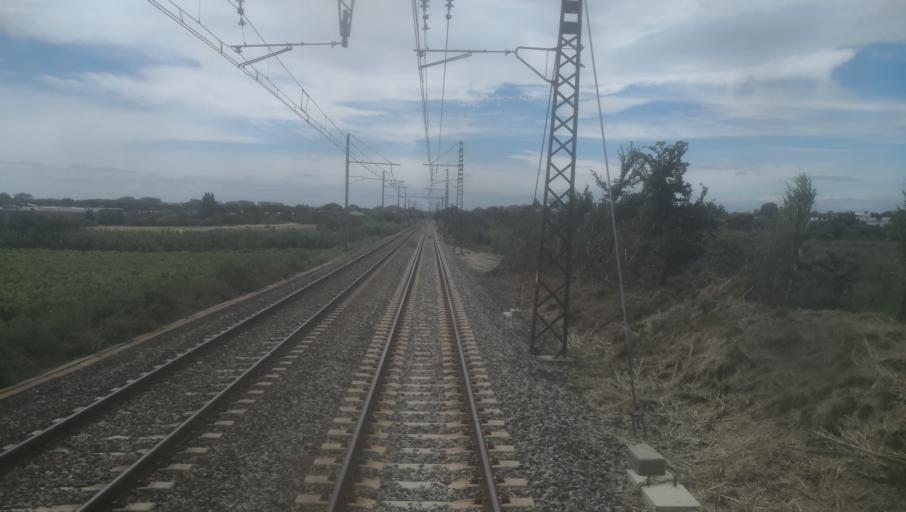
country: FR
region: Languedoc-Roussillon
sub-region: Departement de l'Herault
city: Cers
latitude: 43.3262
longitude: 3.2960
